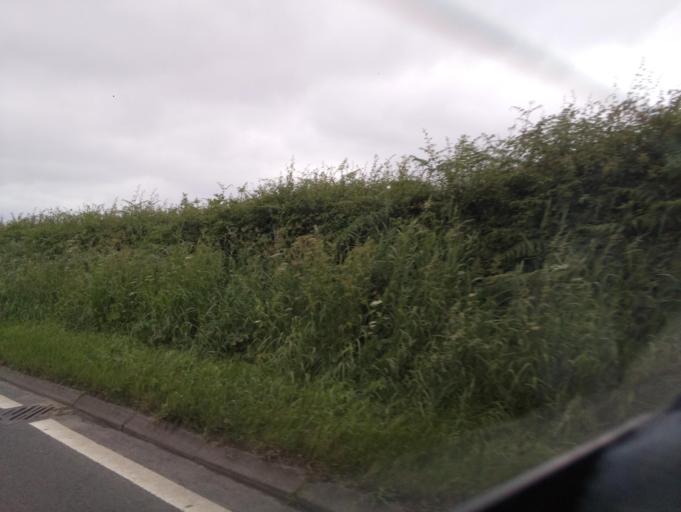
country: GB
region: England
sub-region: Derbyshire
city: Yeldersley
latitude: 52.9652
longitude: -1.6068
